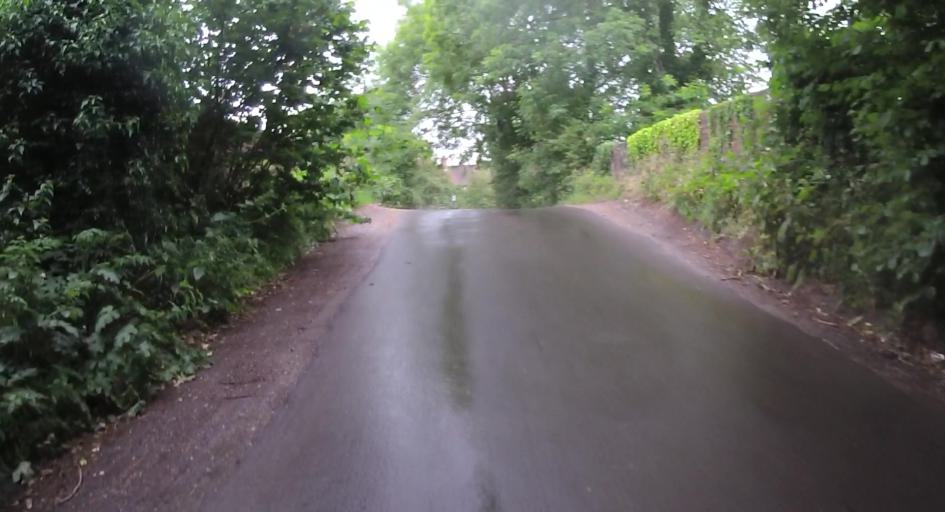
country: GB
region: England
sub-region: Hampshire
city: Long Sutton
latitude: 51.1719
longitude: -0.9212
